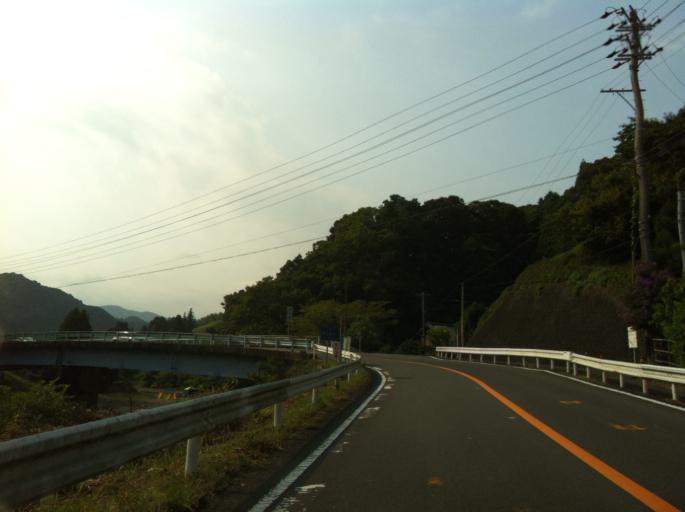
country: JP
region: Shizuoka
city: Fujieda
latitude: 34.9301
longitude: 138.2699
